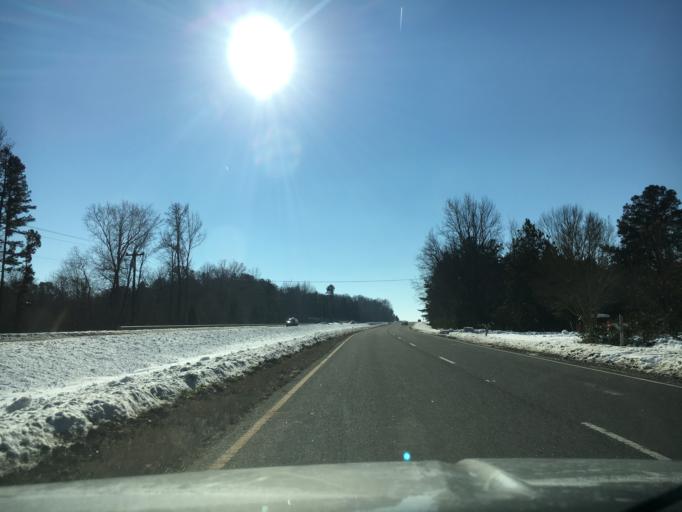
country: US
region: Virginia
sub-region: Nottoway County
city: Crewe
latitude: 37.2838
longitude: -78.1098
